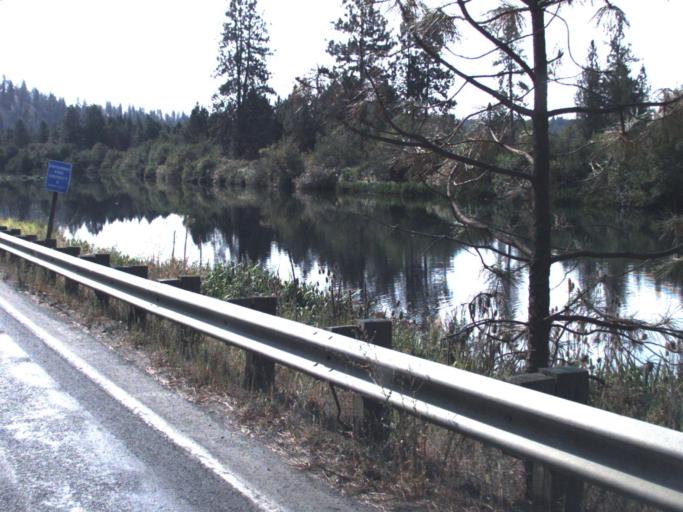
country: US
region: Washington
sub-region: Spokane County
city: Fairwood
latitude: 47.7955
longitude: -117.5335
